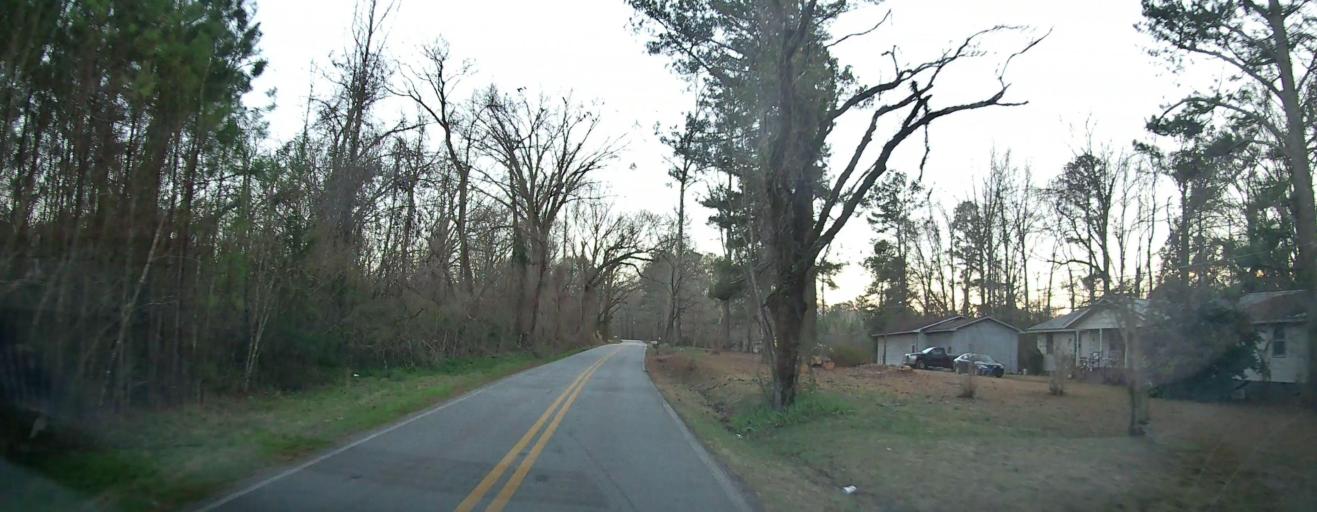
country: US
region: Georgia
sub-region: Troup County
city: La Grange
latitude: 33.0585
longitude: -84.9691
